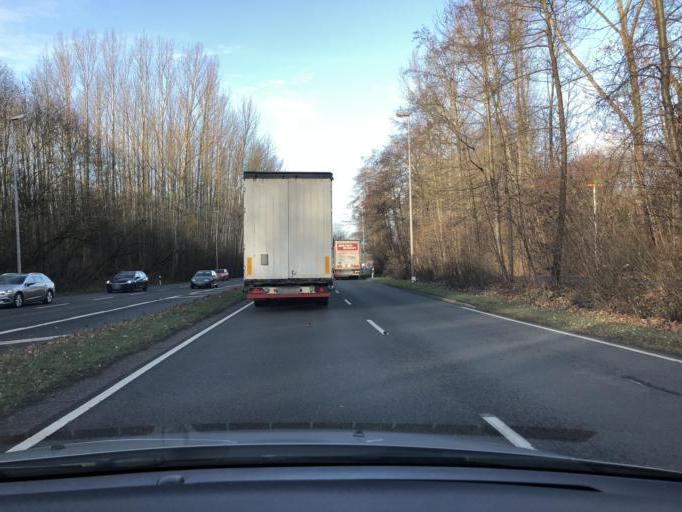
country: DE
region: Saxony
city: Neukirchen
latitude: 50.8058
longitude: 12.8786
